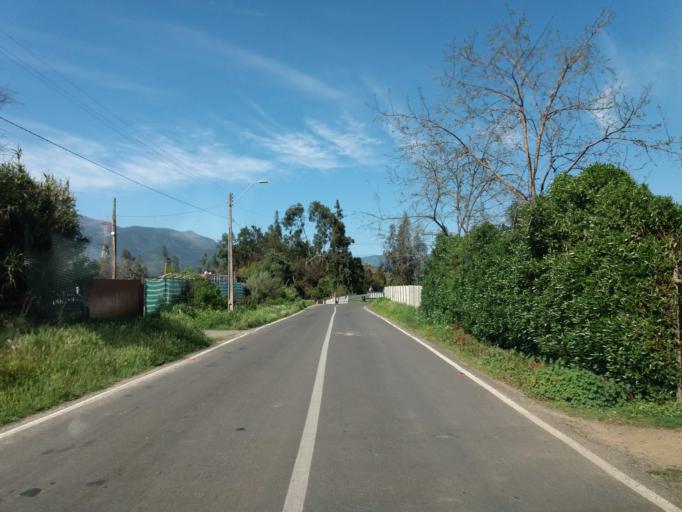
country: CL
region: Valparaiso
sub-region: Provincia de Marga Marga
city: Limache
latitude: -33.0038
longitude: -71.1861
